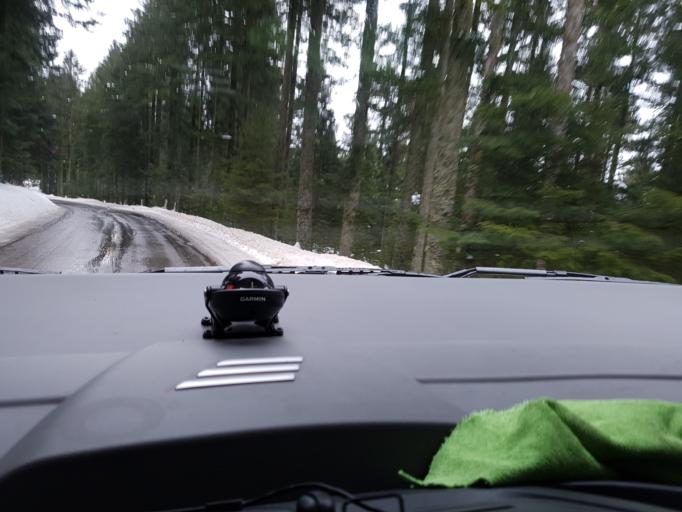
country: FR
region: Lorraine
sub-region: Departement des Vosges
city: Plainfaing
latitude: 48.1467
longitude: 7.0682
